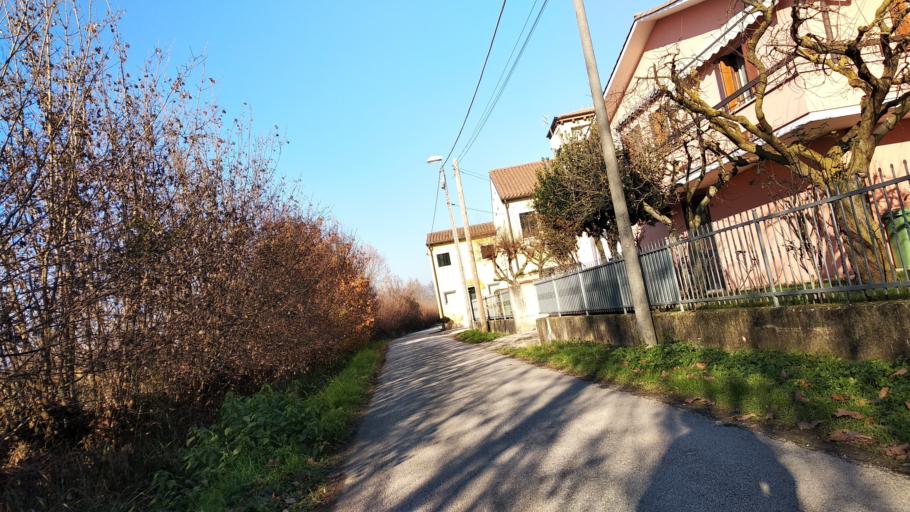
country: IT
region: Veneto
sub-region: Provincia di Vicenza
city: Vicenza
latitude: 45.5788
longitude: 11.5369
